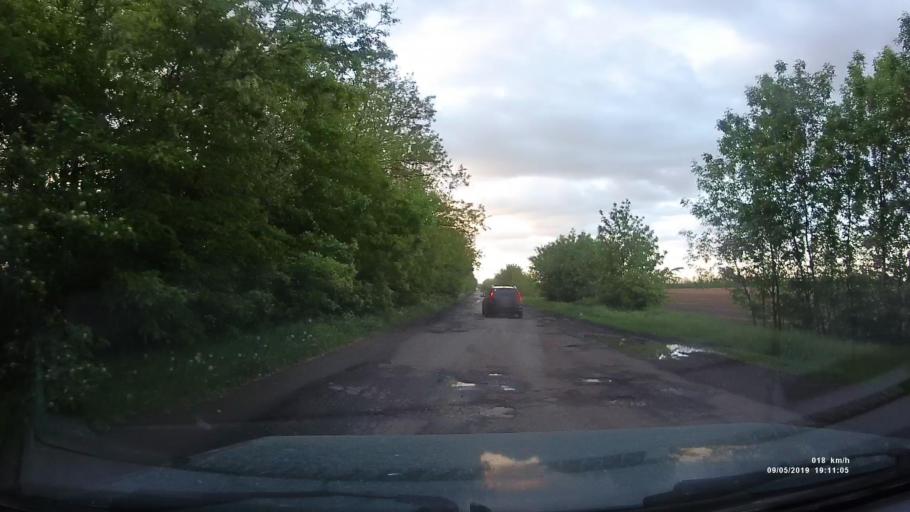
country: RU
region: Krasnodarskiy
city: Kanelovskaya
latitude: 46.7338
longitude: 39.2136
